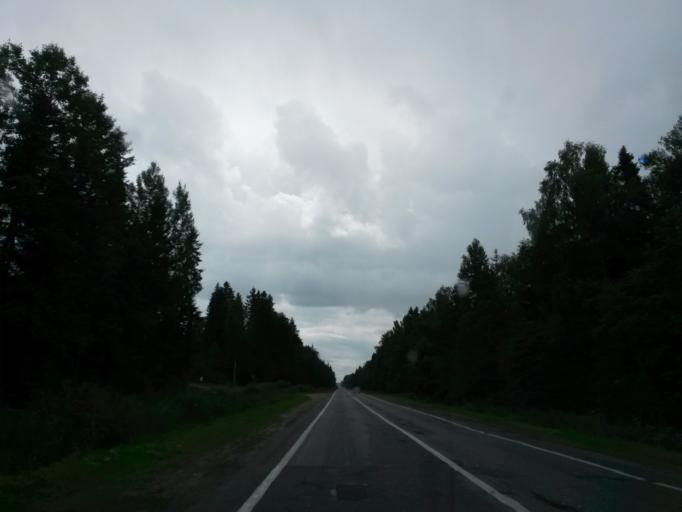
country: RU
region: Jaroslavl
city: Gavrilov-Yam
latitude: 57.4318
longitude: 39.9182
